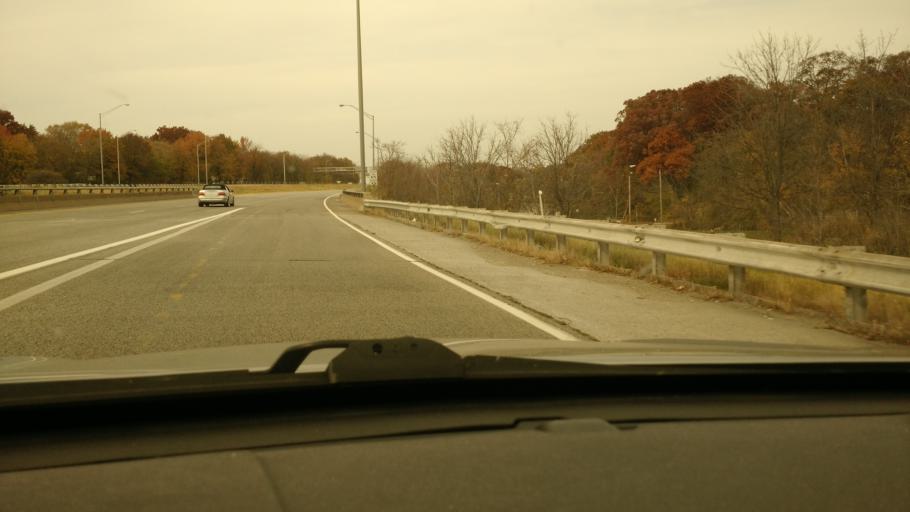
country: US
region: Illinois
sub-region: Rock Island County
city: Moline
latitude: 41.4936
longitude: -90.5059
